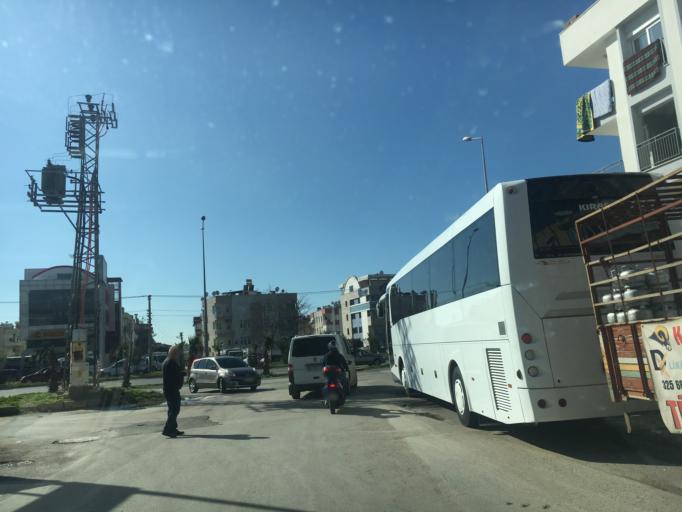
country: TR
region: Antalya
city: Antalya
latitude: 36.9129
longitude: 30.7056
